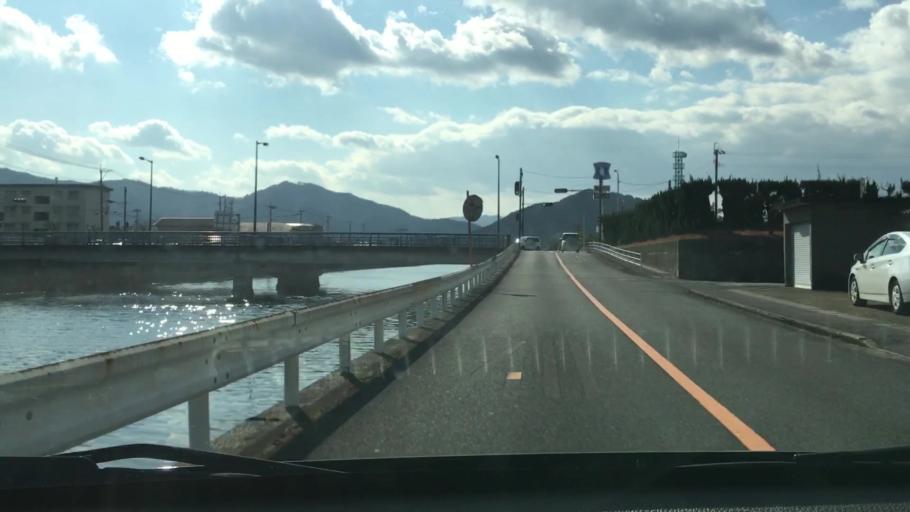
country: JP
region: Oita
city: Saiki
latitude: 32.9568
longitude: 131.9094
